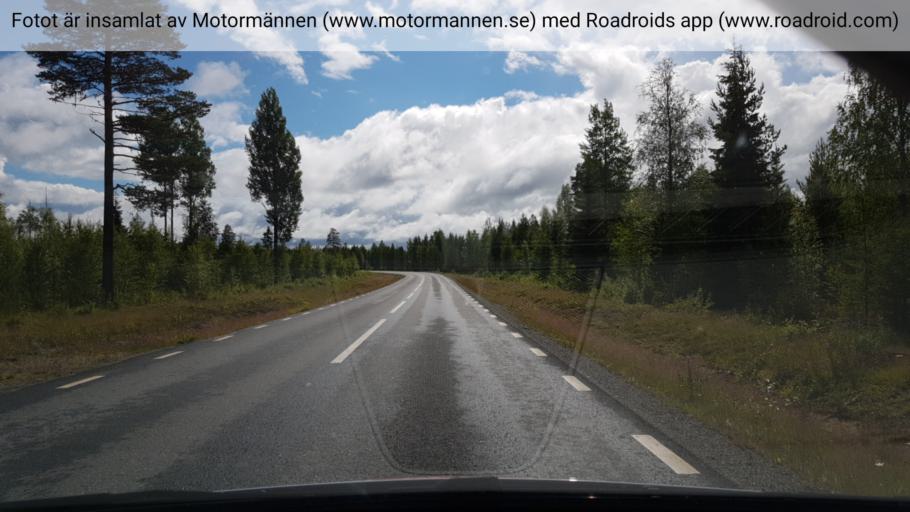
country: SE
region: Vaesterbotten
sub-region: Bjurholms Kommun
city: Bjurholm
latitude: 64.3419
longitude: 19.1471
